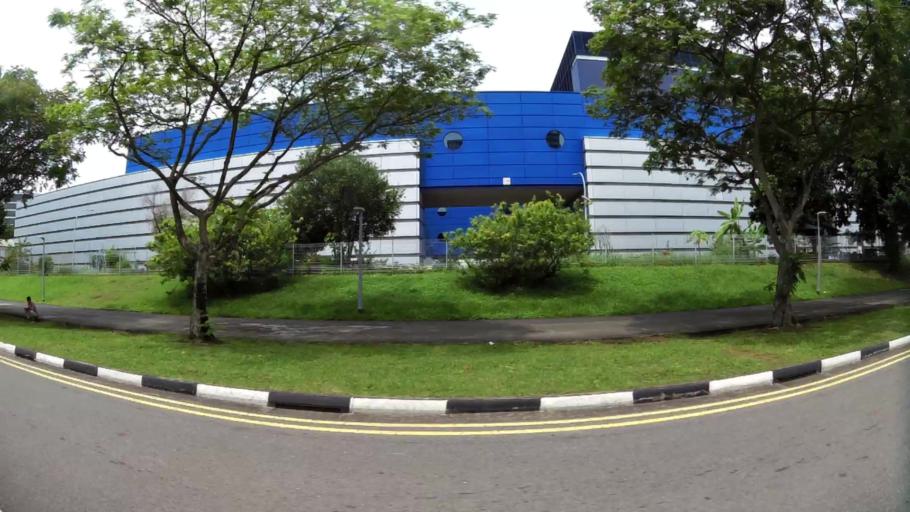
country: MY
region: Johor
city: Kampung Pasir Gudang Baru
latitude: 1.3817
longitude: 103.9352
